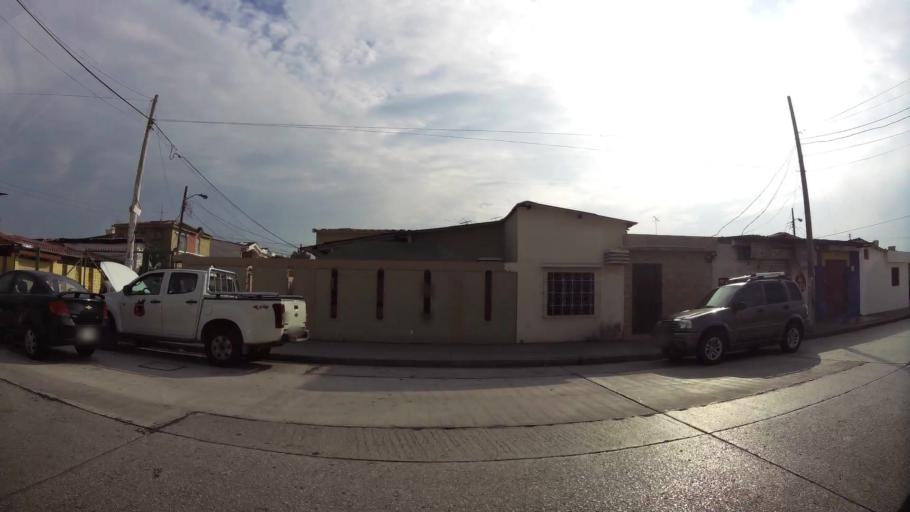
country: EC
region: Guayas
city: Guayaquil
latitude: -2.2424
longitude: -79.9038
